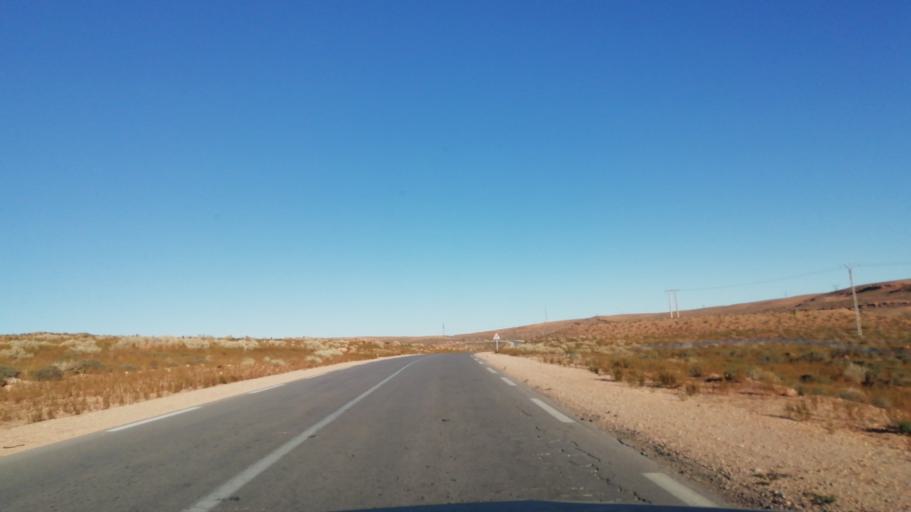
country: DZ
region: El Bayadh
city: El Abiodh Sidi Cheikh
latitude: 33.1681
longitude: 0.4242
